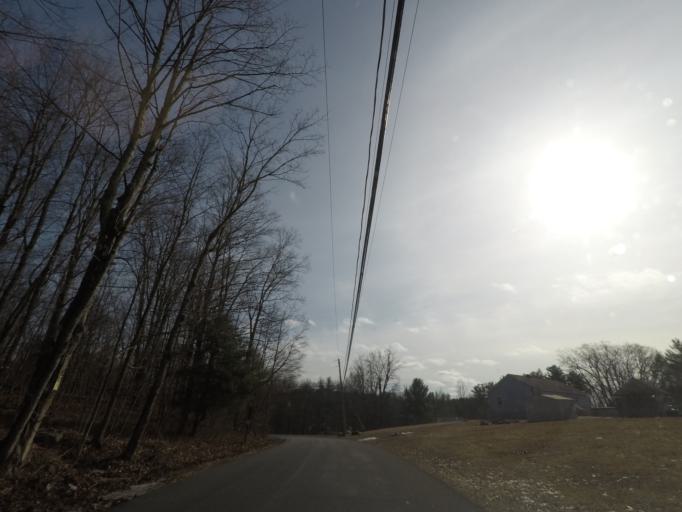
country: US
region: New York
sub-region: Rensselaer County
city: Nassau
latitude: 42.5024
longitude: -73.5510
